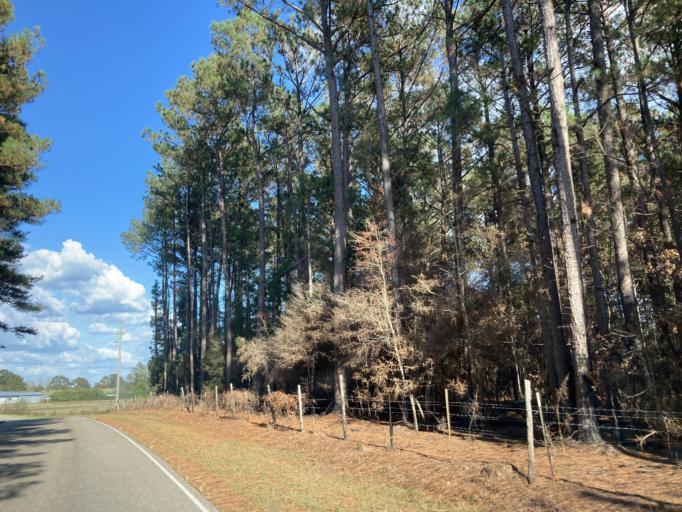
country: US
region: Mississippi
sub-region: Lamar County
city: Sumrall
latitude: 31.4211
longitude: -89.6424
